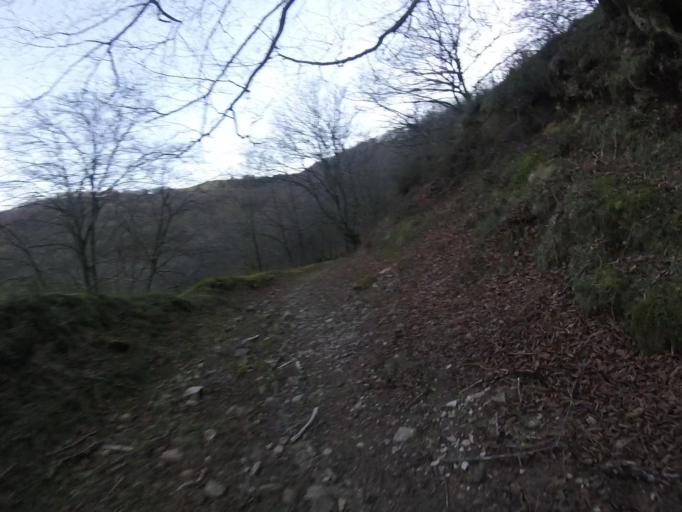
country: ES
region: Navarre
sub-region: Provincia de Navarra
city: Arano
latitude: 43.2526
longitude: -1.8217
